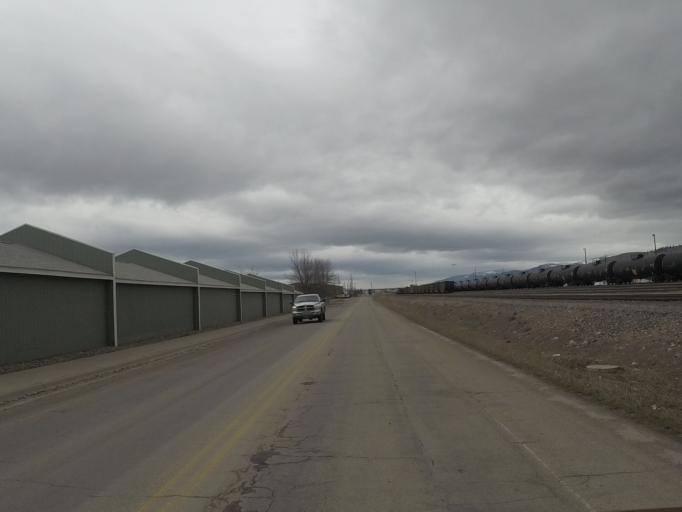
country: US
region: Montana
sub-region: Missoula County
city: Missoula
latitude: 46.8900
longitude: -114.0216
